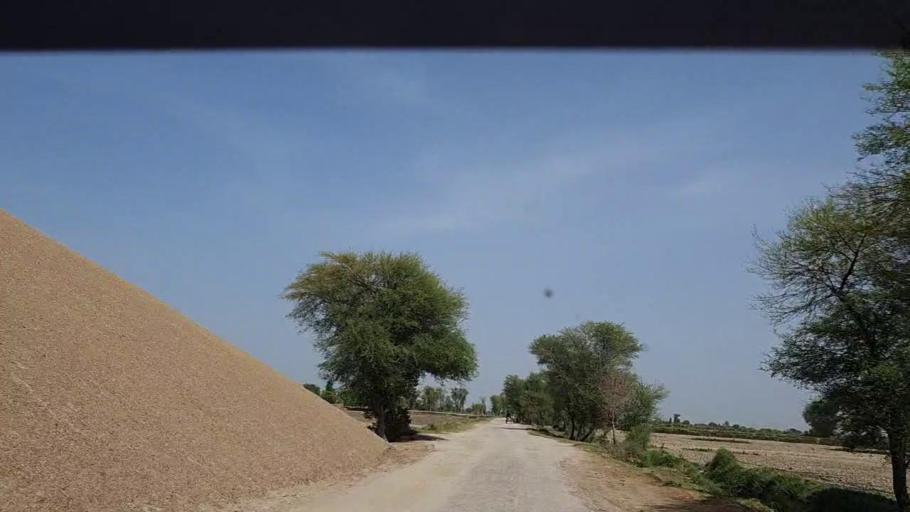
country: PK
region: Sindh
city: Phulji
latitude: 26.9559
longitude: 67.7093
